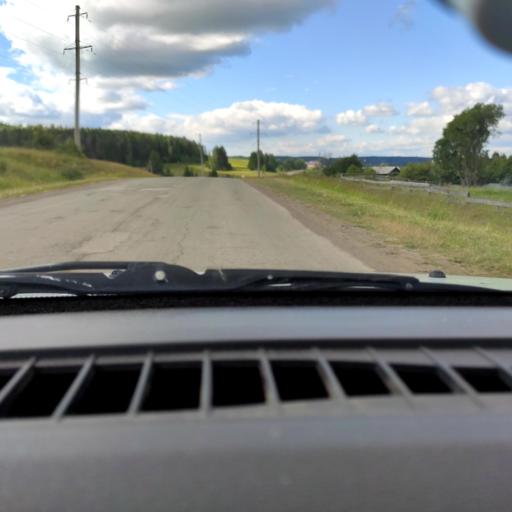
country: RU
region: Perm
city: Uinskoye
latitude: 57.1749
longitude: 56.5610
